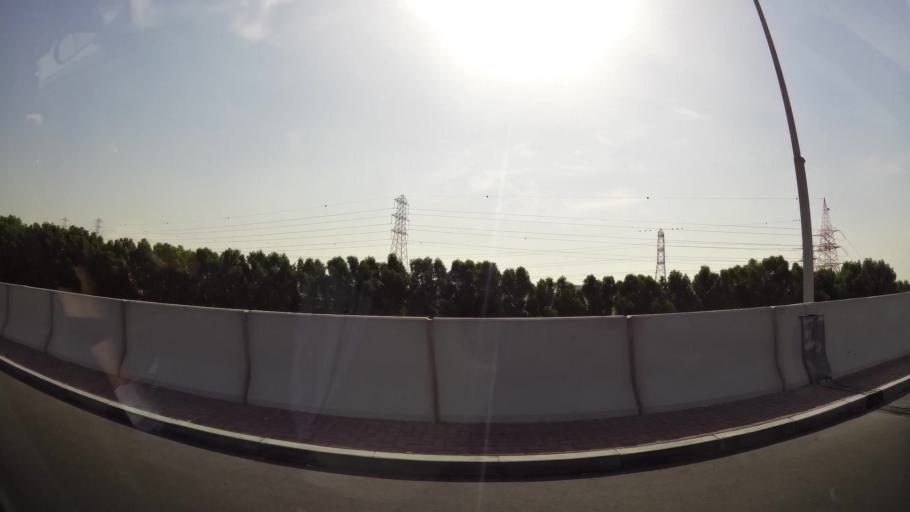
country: AE
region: Ash Shariqah
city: Sharjah
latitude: 25.2370
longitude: 55.4045
